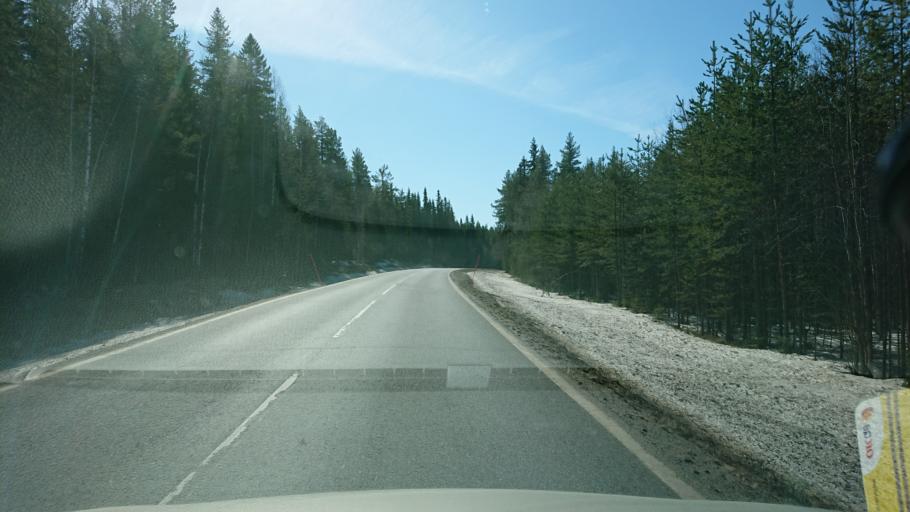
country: SE
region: Vaesterbotten
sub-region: Dorotea Kommun
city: Dorotea
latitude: 64.0494
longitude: 16.2588
